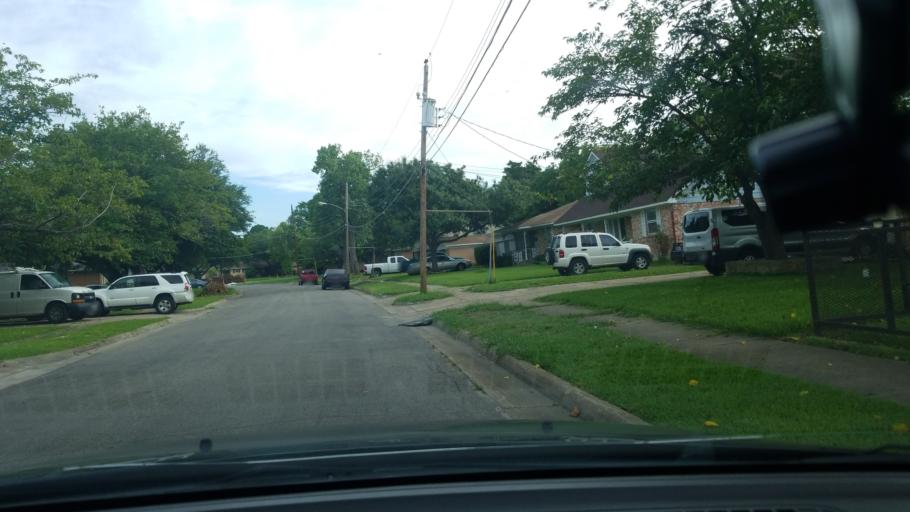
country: US
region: Texas
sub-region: Dallas County
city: Balch Springs
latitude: 32.7541
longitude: -96.6638
